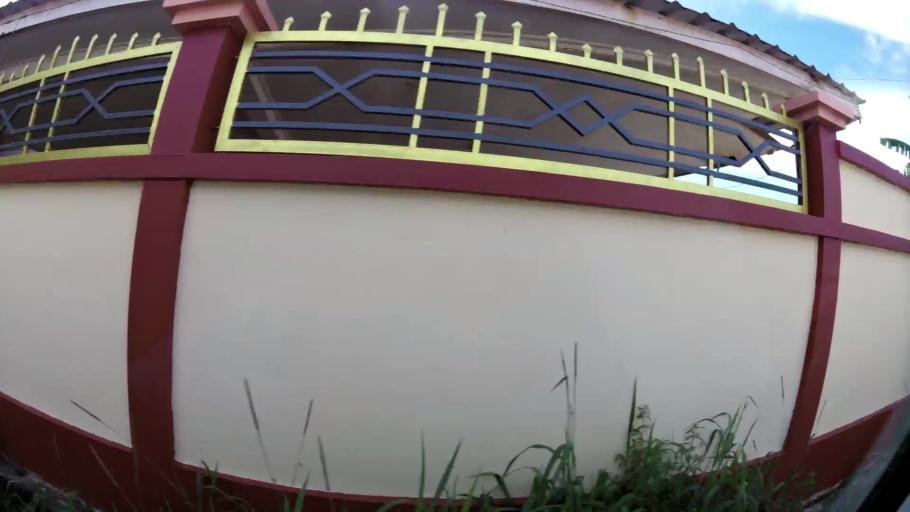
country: BN
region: Brunei and Muara
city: Bandar Seri Begawan
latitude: 4.9855
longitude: 115.0230
